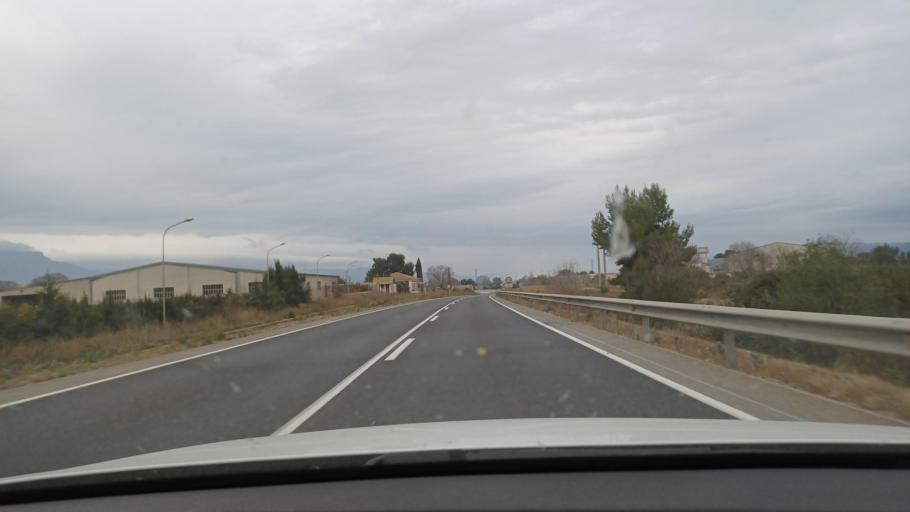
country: ES
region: Catalonia
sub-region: Provincia de Tarragona
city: Santa Barbara
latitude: 40.7133
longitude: 0.5065
